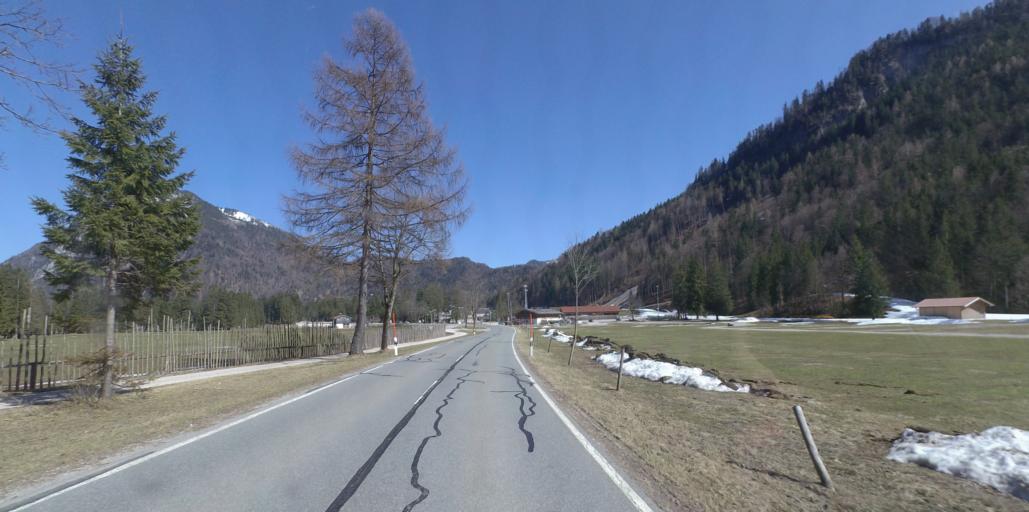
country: DE
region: Bavaria
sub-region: Upper Bavaria
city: Ruhpolding
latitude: 47.7153
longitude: 12.6389
